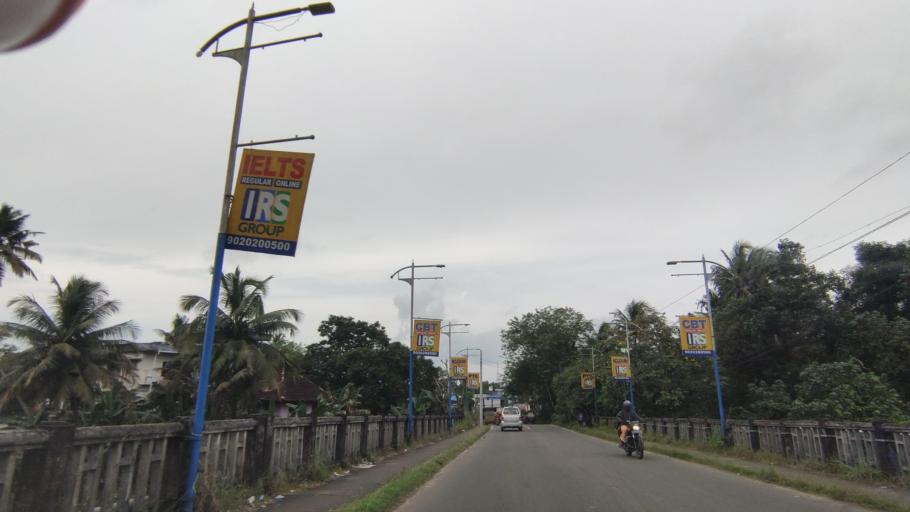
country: IN
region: Kerala
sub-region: Kottayam
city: Kottayam
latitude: 9.6012
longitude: 76.5177
